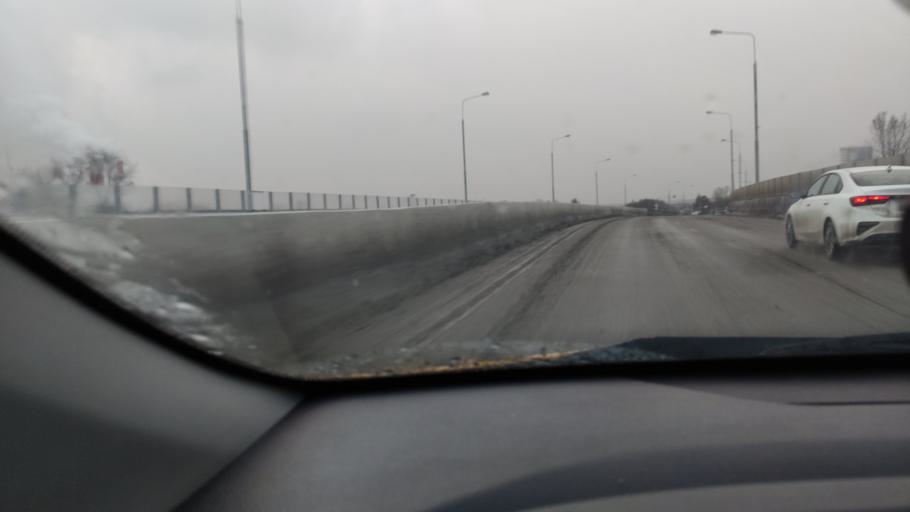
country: RU
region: Moscow
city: Annino
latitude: 55.5867
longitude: 37.6136
